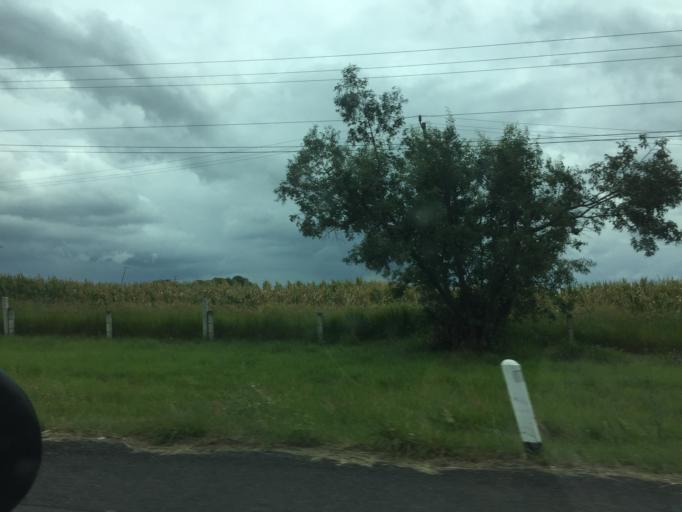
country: MX
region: Jalisco
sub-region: Tonala
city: Mismaloya (Fraccionamiento Pedregal de Santa Martha)
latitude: 20.6062
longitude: -103.1333
